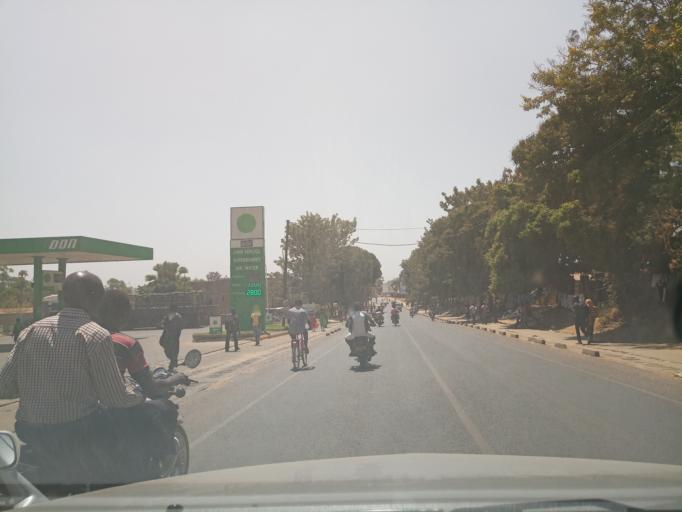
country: UG
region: Northern Region
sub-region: Arua District
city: Arua
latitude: 3.0112
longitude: 30.9128
